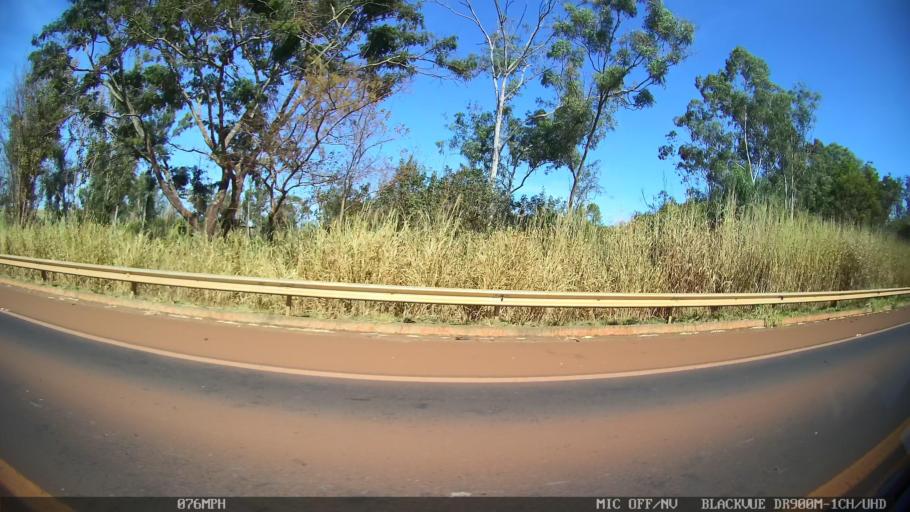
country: BR
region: Sao Paulo
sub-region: Sao Joaquim Da Barra
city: Sao Joaquim da Barra
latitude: -20.5469
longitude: -47.7688
